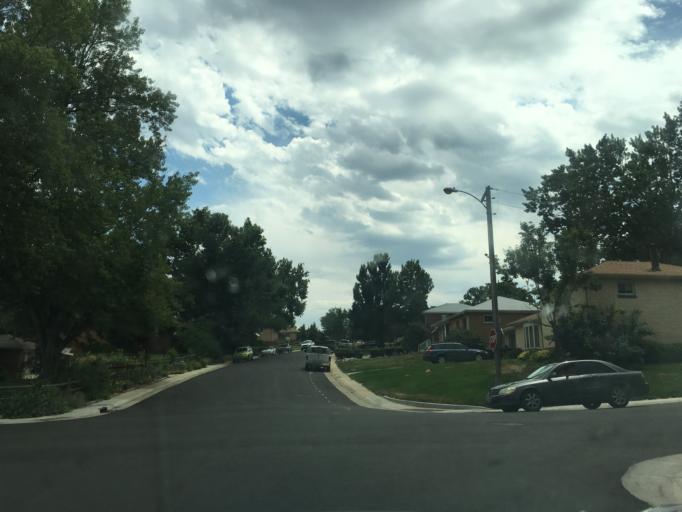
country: US
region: Colorado
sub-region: Arapahoe County
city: Sheridan
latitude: 39.6767
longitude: -105.0497
